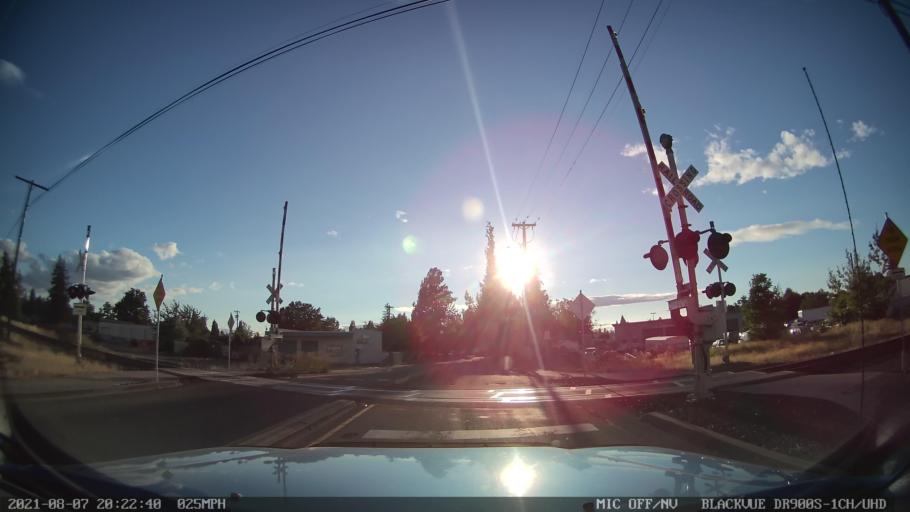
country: US
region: Oregon
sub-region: Marion County
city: Salem
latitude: 44.9564
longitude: -123.0159
